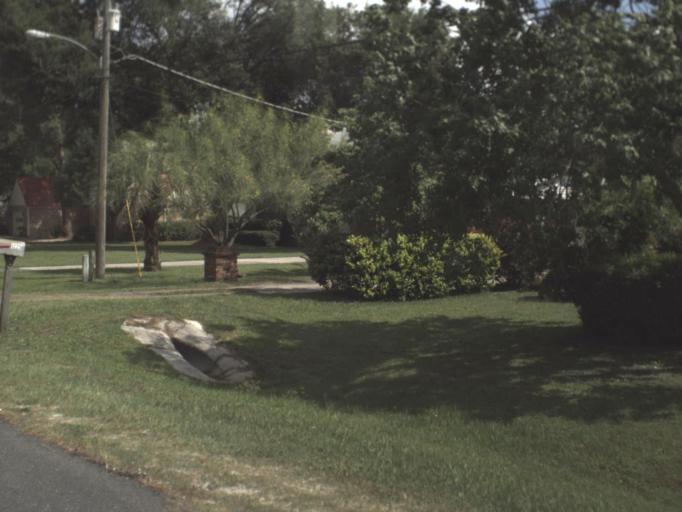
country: US
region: Florida
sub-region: Baker County
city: Macclenny
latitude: 30.2698
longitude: -82.1153
